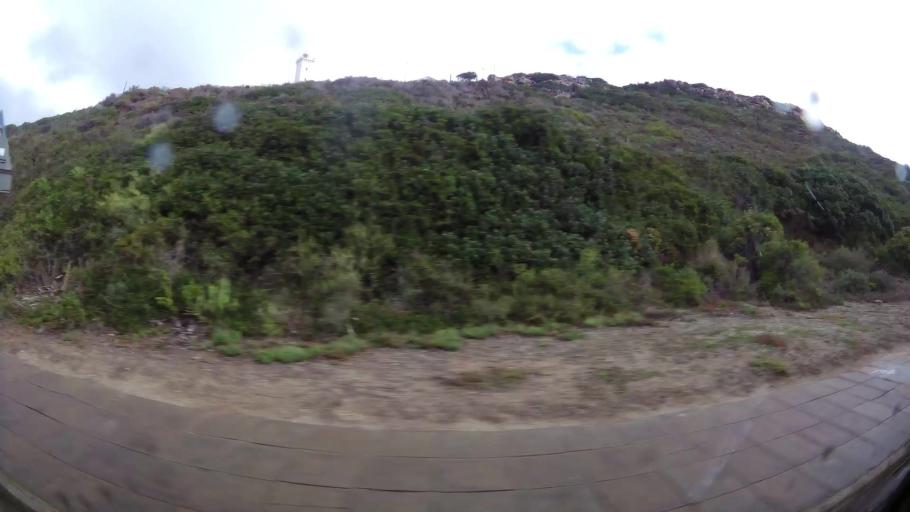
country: ZA
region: Western Cape
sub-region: Eden District Municipality
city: Mossel Bay
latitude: -34.1849
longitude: 22.1567
